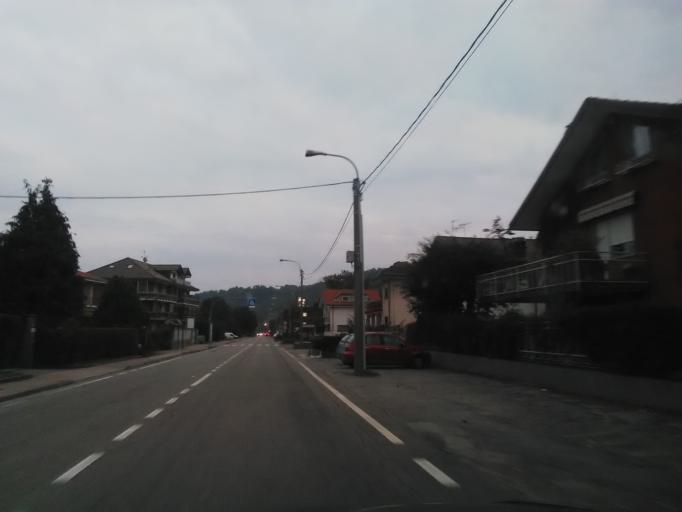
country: IT
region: Piedmont
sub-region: Provincia di Vercelli
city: Serravalle Sesia
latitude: 45.6773
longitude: 8.3196
